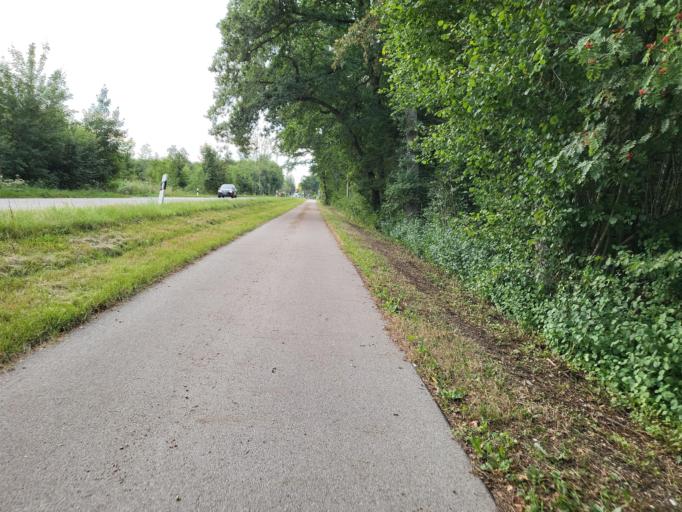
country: DE
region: Bavaria
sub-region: Upper Bavaria
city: Hohenkirchen-Siegertsbrunn
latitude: 48.0113
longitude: 11.7196
